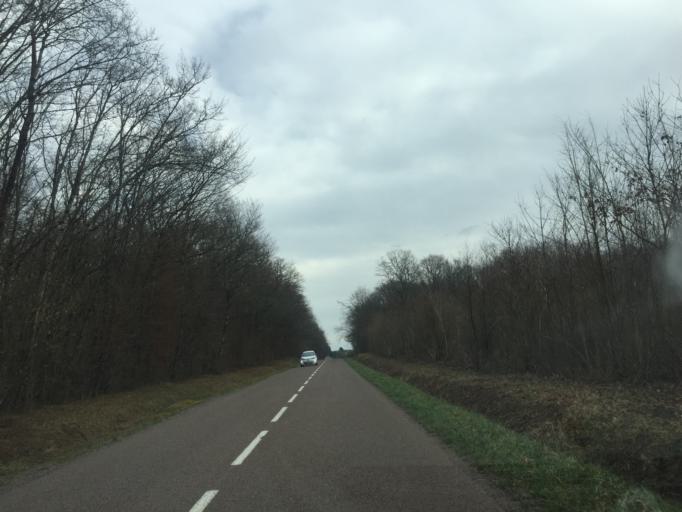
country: FR
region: Franche-Comte
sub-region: Departement du Jura
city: Chaussin
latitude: 46.9220
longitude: 5.4971
